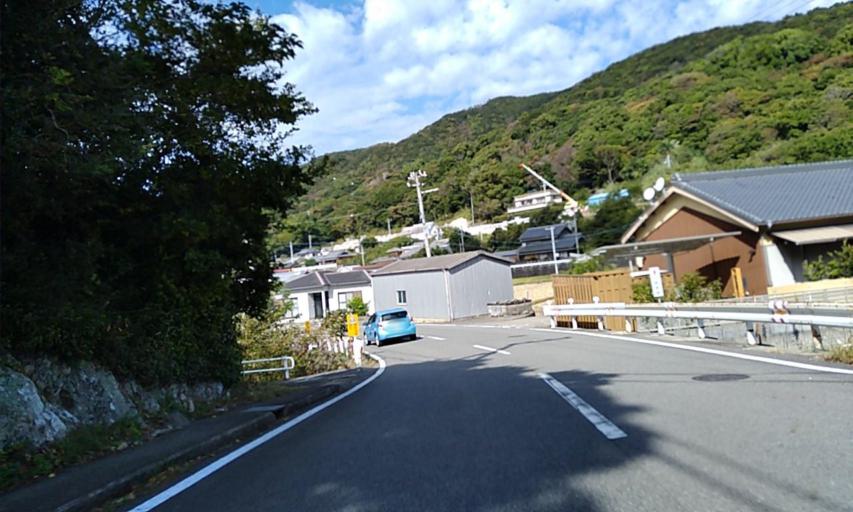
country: JP
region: Wakayama
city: Gobo
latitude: 33.9680
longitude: 135.0891
